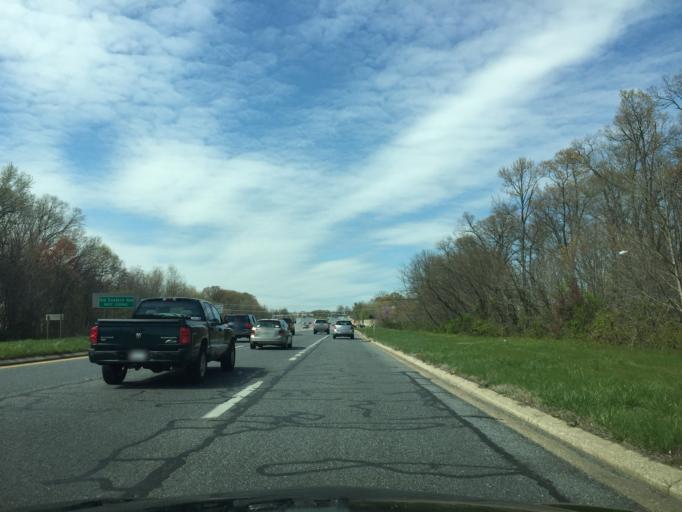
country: US
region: Maryland
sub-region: Baltimore County
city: Essex
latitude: 39.3122
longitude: -76.4530
